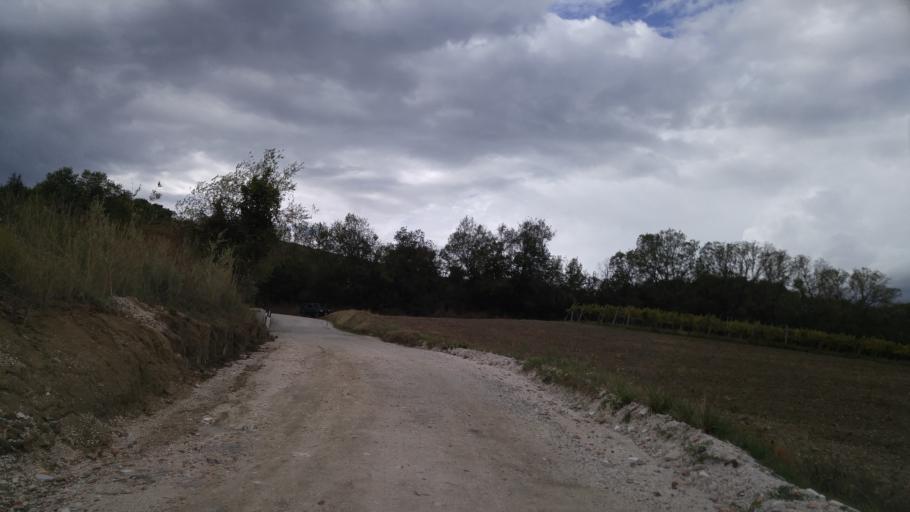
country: IT
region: The Marches
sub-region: Provincia di Pesaro e Urbino
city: Cartoceto
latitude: 43.7882
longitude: 12.8824
